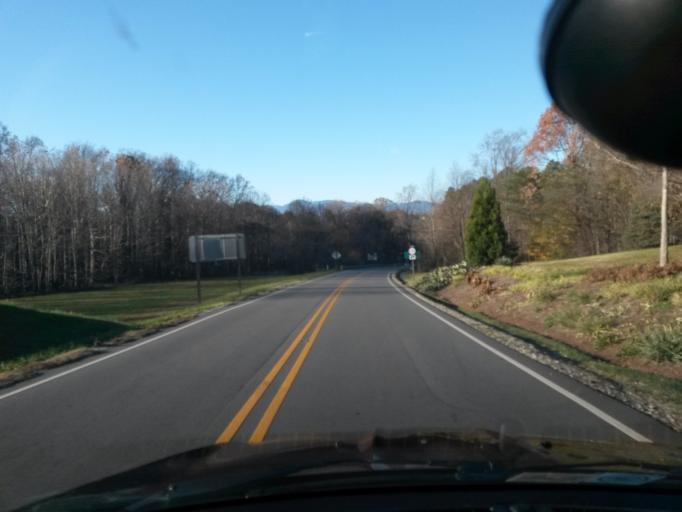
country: US
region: Virginia
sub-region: Amherst County
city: Amherst
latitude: 37.5900
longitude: -79.0511
